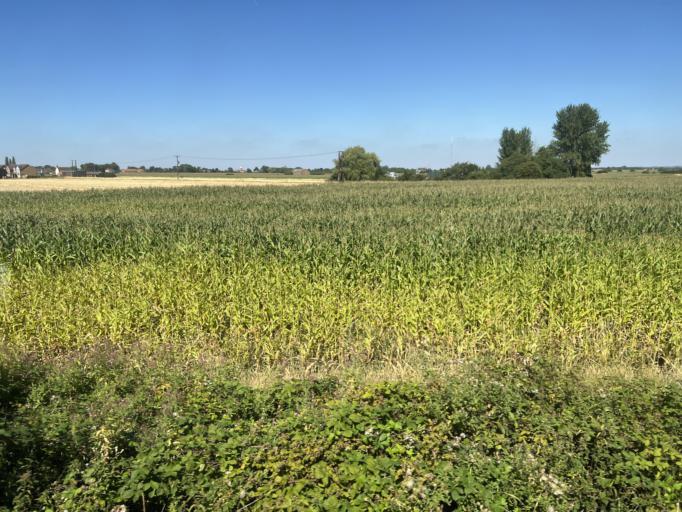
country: GB
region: England
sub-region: Lincolnshire
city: Boston
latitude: 53.0382
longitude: 0.0305
